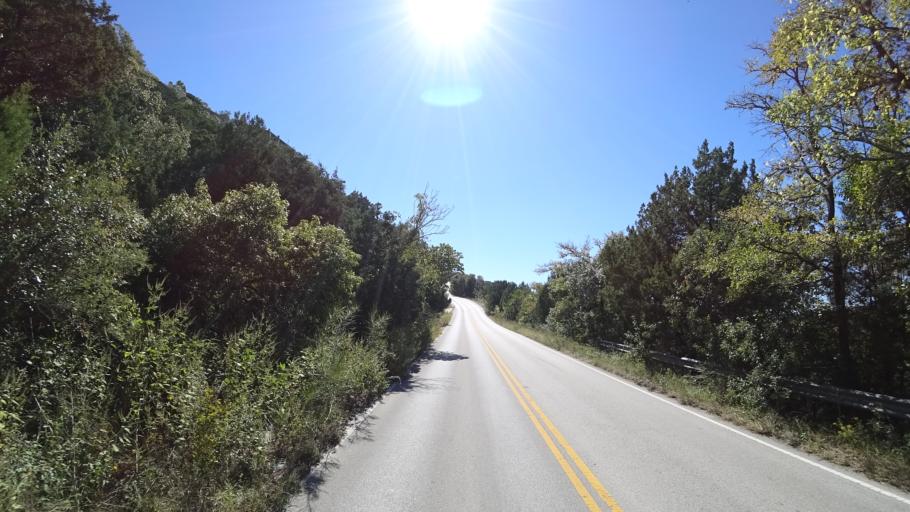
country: US
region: Texas
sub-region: Travis County
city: West Lake Hills
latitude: 30.3263
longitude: -97.7747
